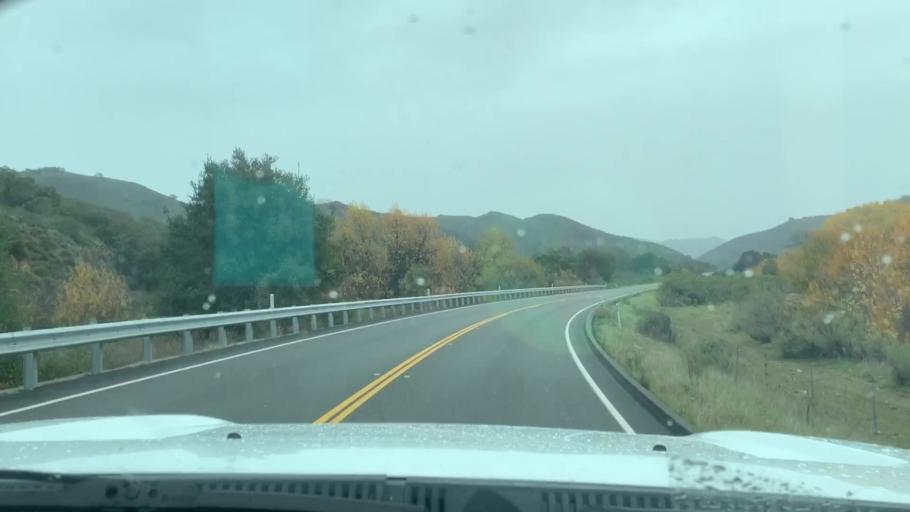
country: US
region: California
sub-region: Santa Barbara County
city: Santa Maria
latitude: 35.0307
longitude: -120.2492
